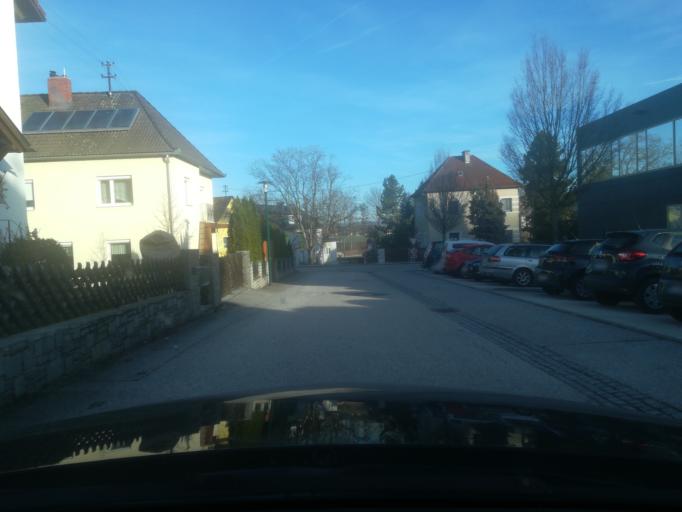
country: AT
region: Upper Austria
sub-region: Wels-Land
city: Marchtrenk
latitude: 48.1626
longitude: 14.1243
